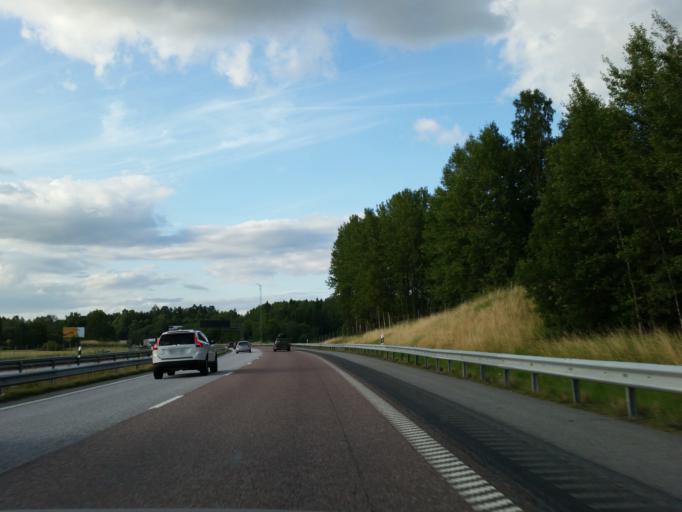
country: SE
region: Stockholm
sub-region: Sodertalje Kommun
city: Pershagen
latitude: 59.1430
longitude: 17.6496
